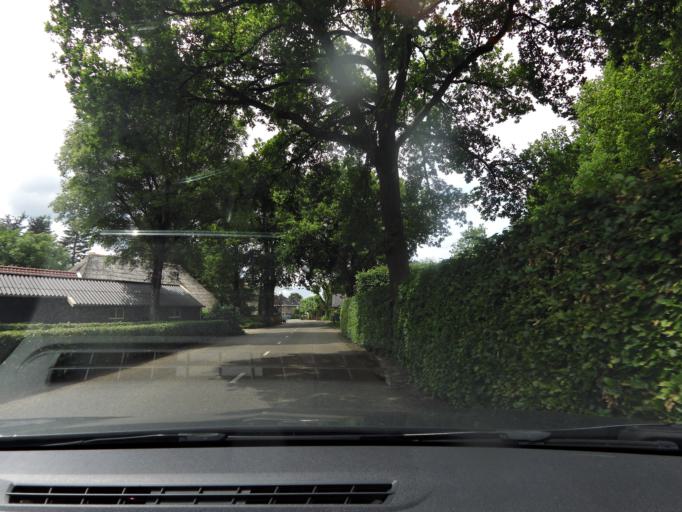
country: NL
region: Gelderland
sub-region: Gemeente Apeldoorn
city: Uddel
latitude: 52.2570
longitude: 5.7849
